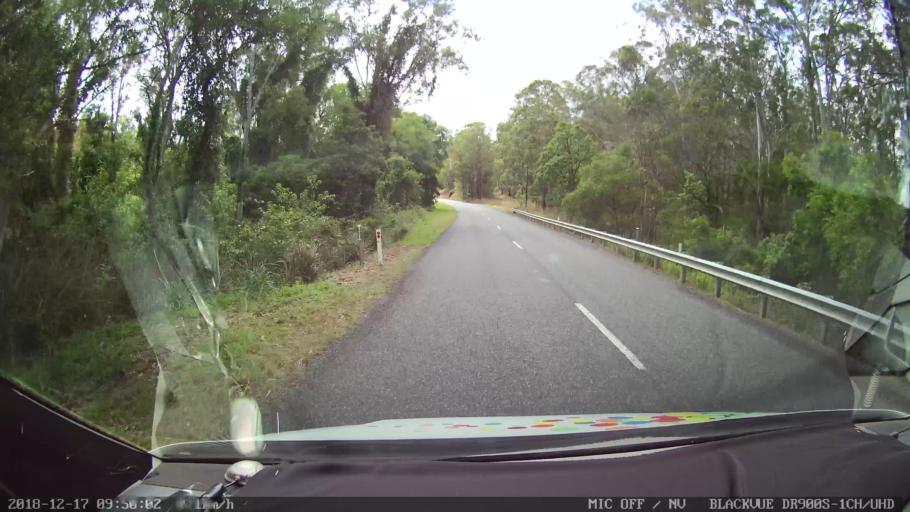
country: AU
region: New South Wales
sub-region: Tenterfield Municipality
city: Carrolls Creek
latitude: -28.9261
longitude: 152.3594
